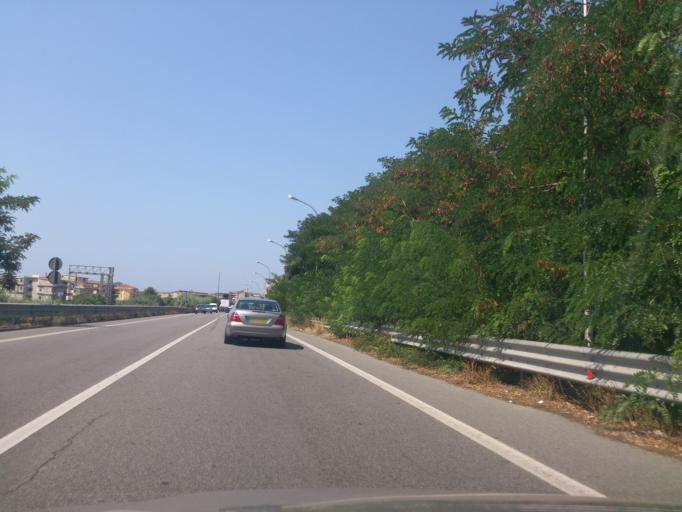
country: IT
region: Calabria
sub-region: Provincia di Reggio Calabria
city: Caulonia Marina
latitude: 38.3471
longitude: 16.4715
